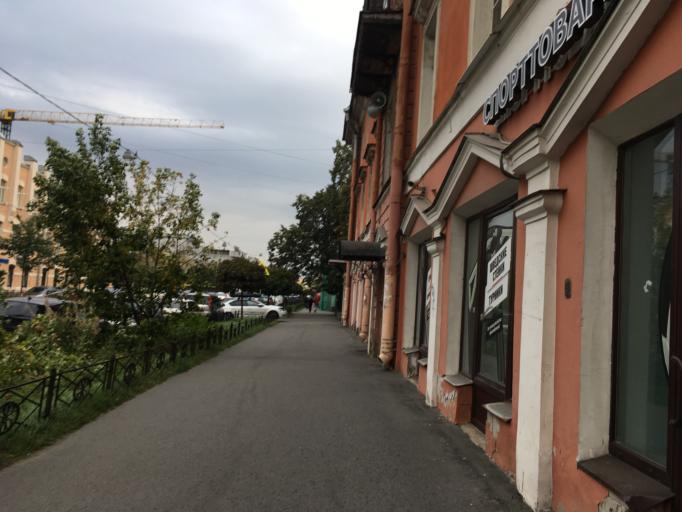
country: RU
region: St.-Petersburg
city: Centralniy
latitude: 59.9174
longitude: 30.3425
